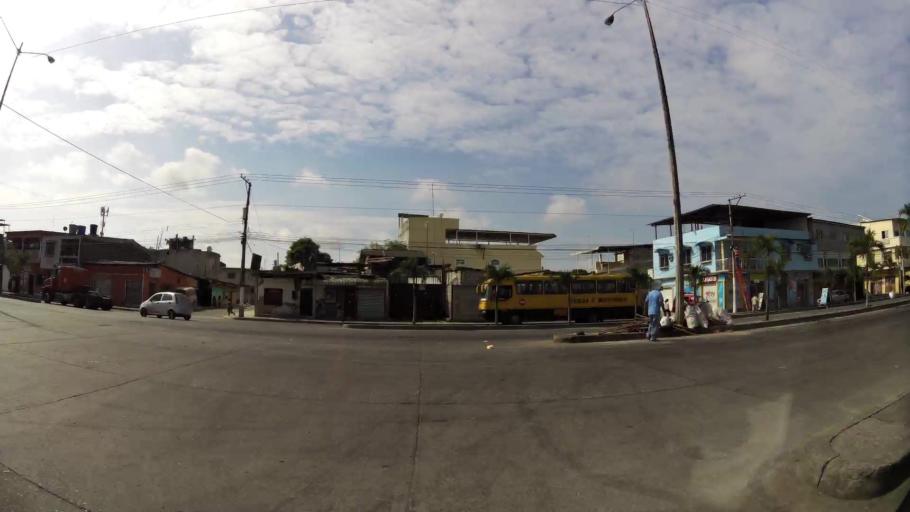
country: EC
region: Guayas
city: Guayaquil
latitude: -2.2648
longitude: -79.8940
